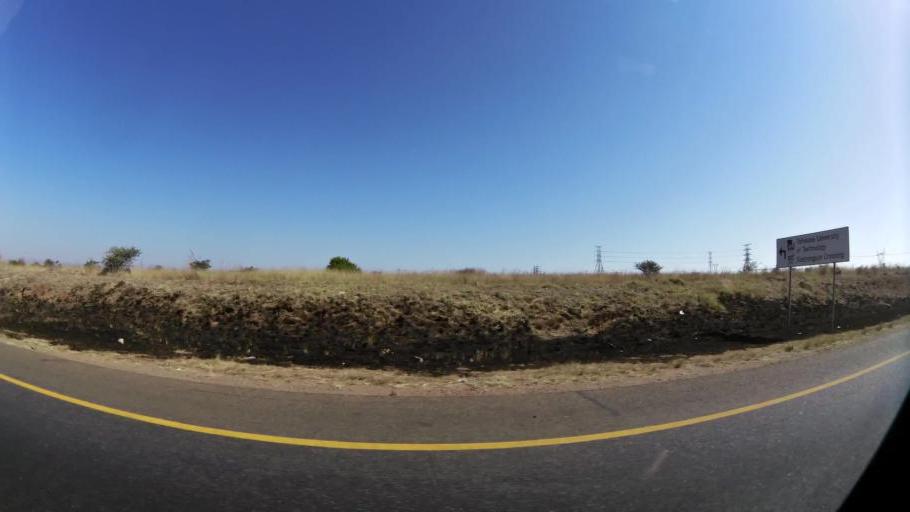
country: ZA
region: Gauteng
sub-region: City of Tshwane Metropolitan Municipality
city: Mabopane
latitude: -25.5657
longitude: 28.1075
